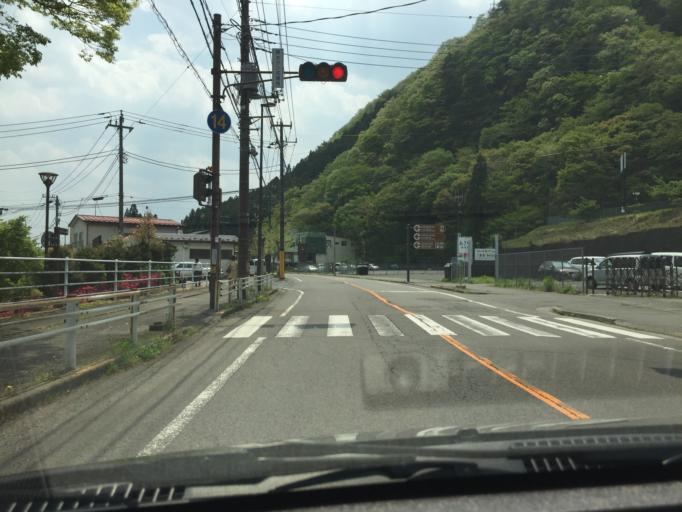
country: JP
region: Tochigi
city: Imaichi
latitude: 36.8353
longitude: 139.7183
